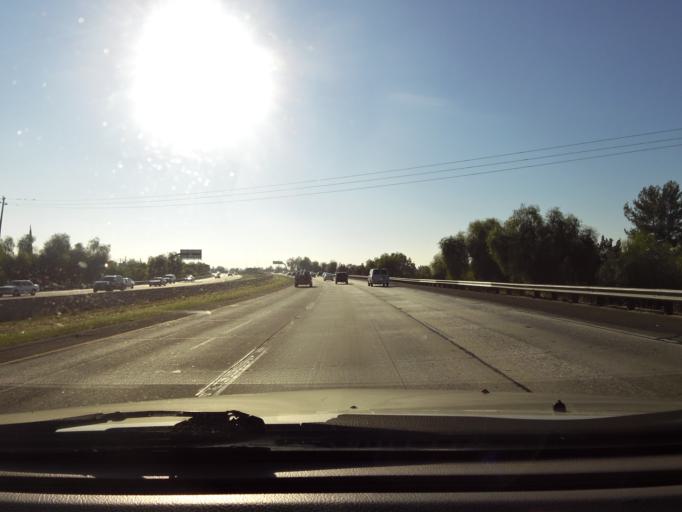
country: US
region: California
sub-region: Fresno County
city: Fresno
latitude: 36.7704
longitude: -119.7841
